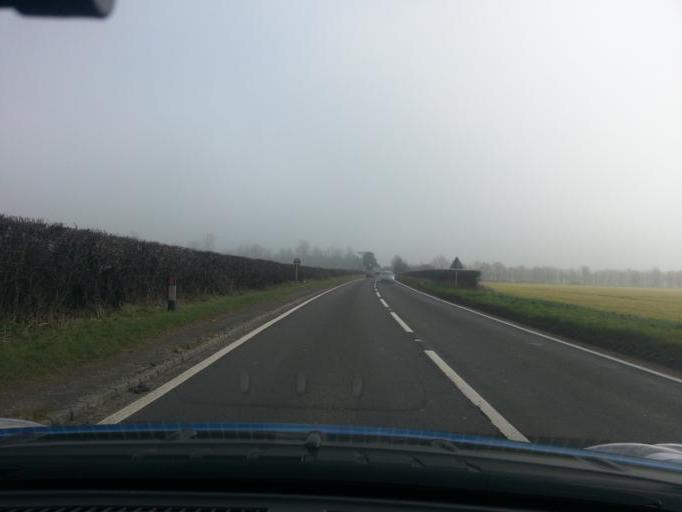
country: GB
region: England
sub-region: Oxfordshire
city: Stanford in the Vale
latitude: 51.6736
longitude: -1.5351
